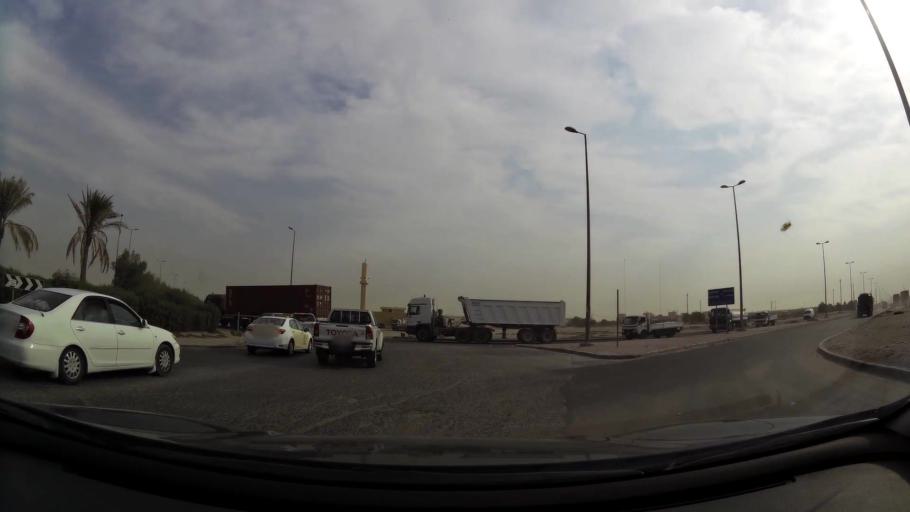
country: KW
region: Muhafazat al Jahra'
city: Al Jahra'
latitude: 29.3155
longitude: 47.7464
